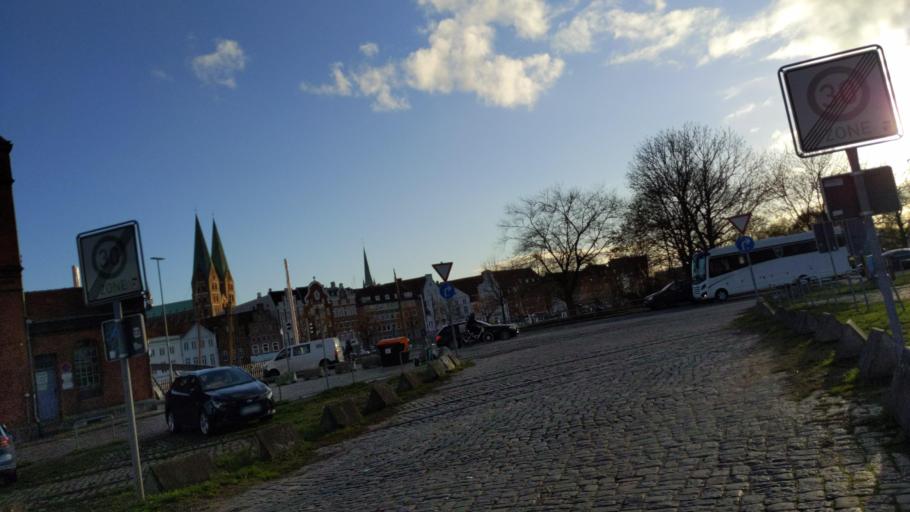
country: DE
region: Schleswig-Holstein
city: Luebeck
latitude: 53.8735
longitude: 10.6819
